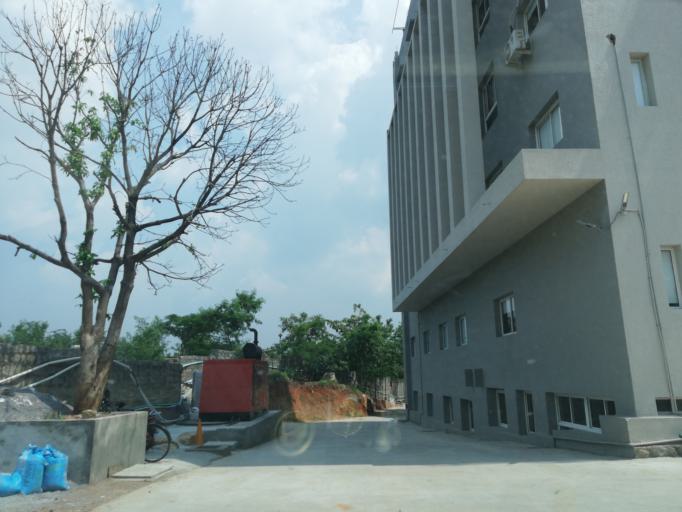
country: IN
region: Telangana
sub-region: Rangareddi
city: Kukatpalli
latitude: 17.4356
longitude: 78.3598
